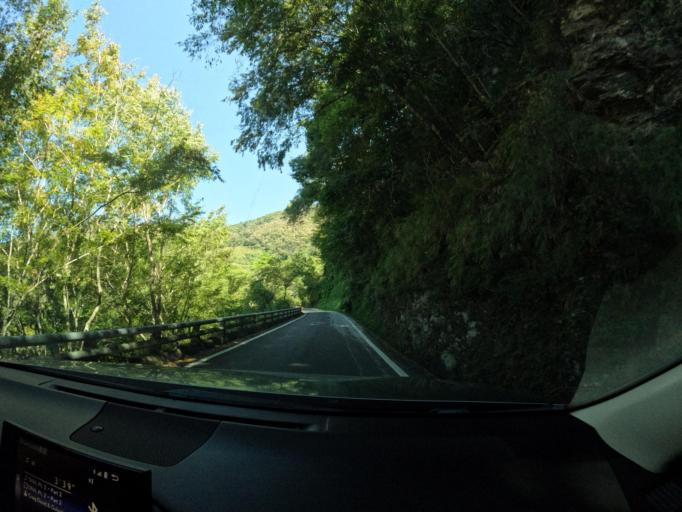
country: TW
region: Taiwan
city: Yujing
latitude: 23.2713
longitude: 120.8448
